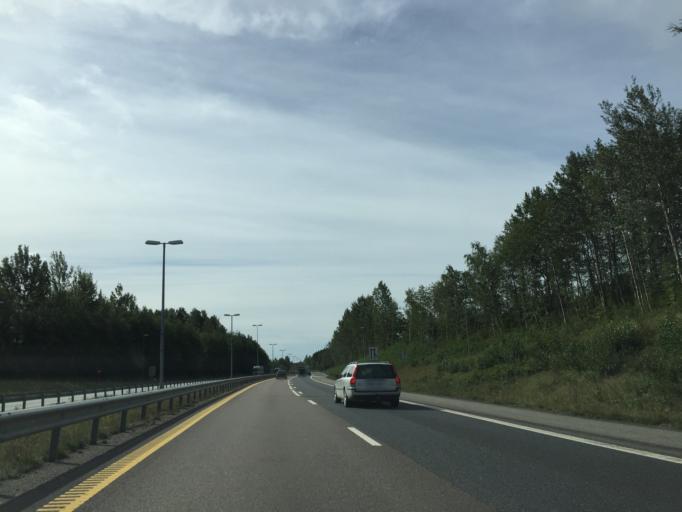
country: NO
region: Akershus
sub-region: As
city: As
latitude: 59.6622
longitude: 10.7450
